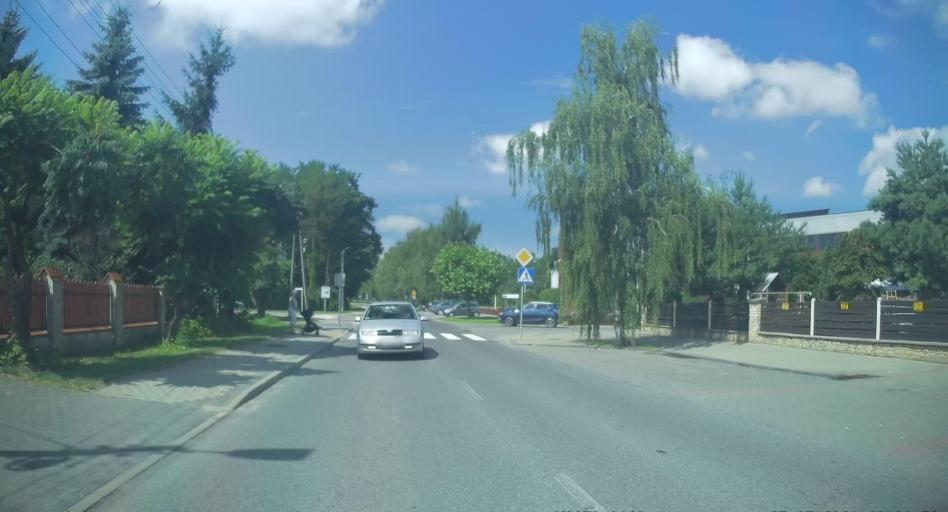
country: PL
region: Lodz Voivodeship
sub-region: Powiat rawski
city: Rawa Mazowiecka
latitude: 51.7531
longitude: 20.2346
